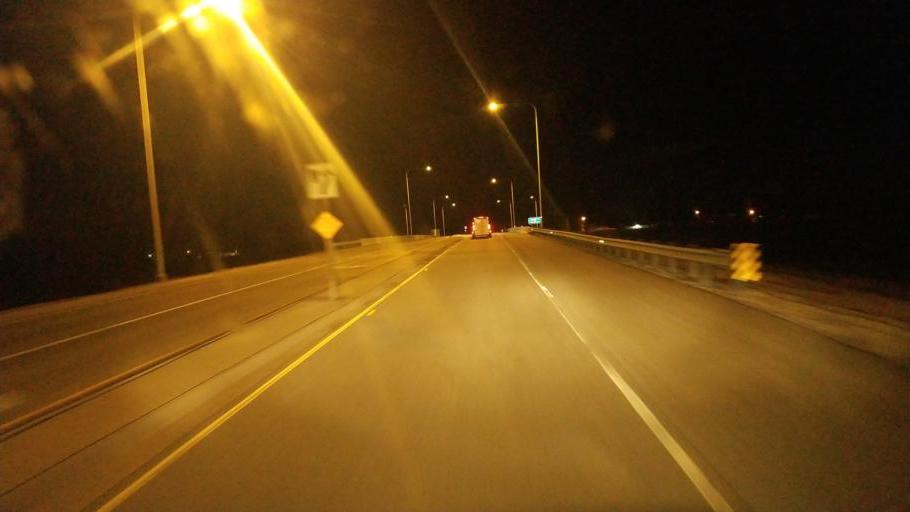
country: US
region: Illinois
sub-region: Henderson County
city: Oquawka
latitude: 40.8431
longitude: -90.9035
